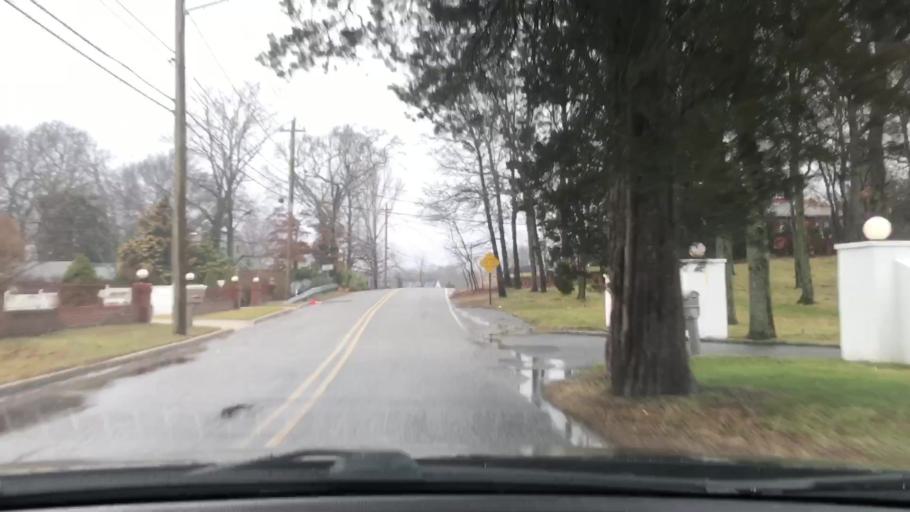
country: US
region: New York
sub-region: Suffolk County
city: Centereach
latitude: 40.8389
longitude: -73.0861
